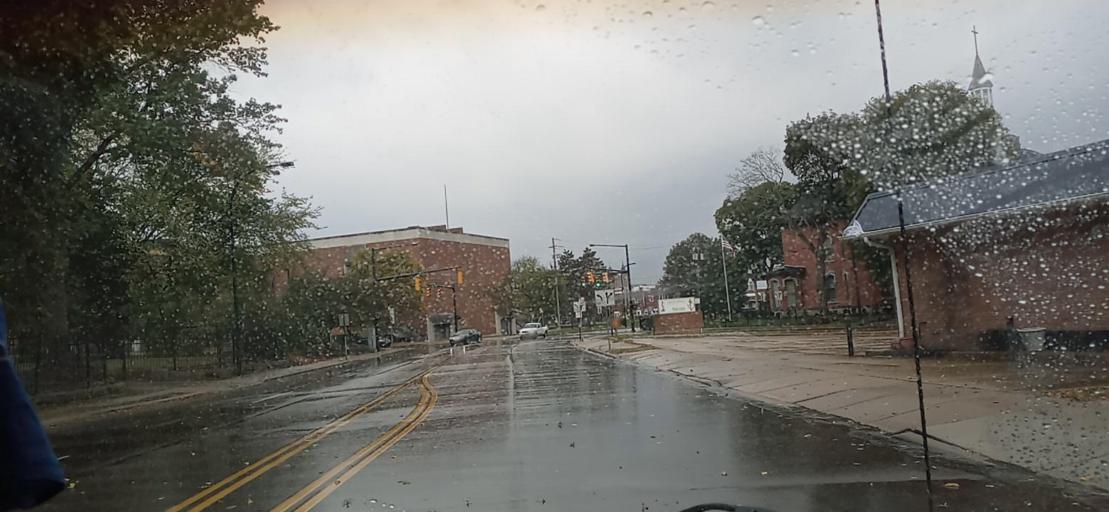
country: US
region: Ohio
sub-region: Summit County
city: Akron
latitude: 41.0802
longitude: -81.5081
